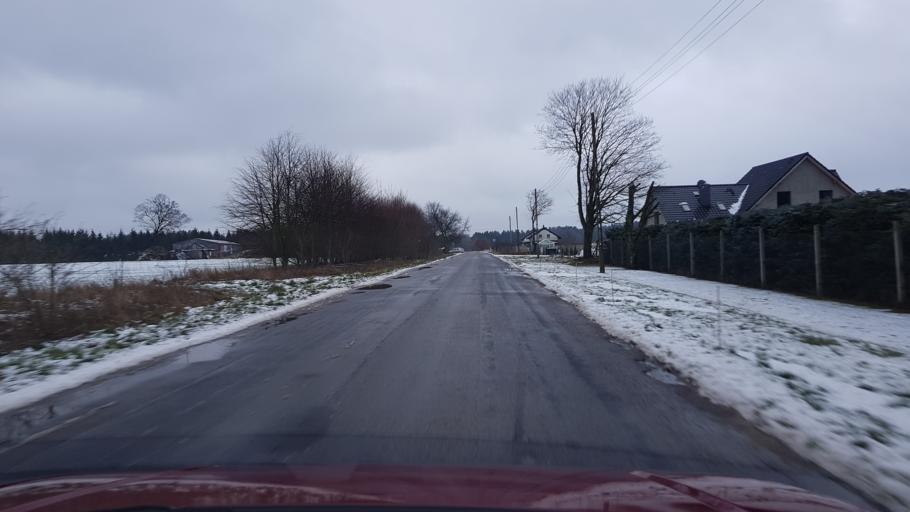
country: PL
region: West Pomeranian Voivodeship
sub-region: Powiat goleniowski
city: Nowogard
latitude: 53.6476
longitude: 15.1229
